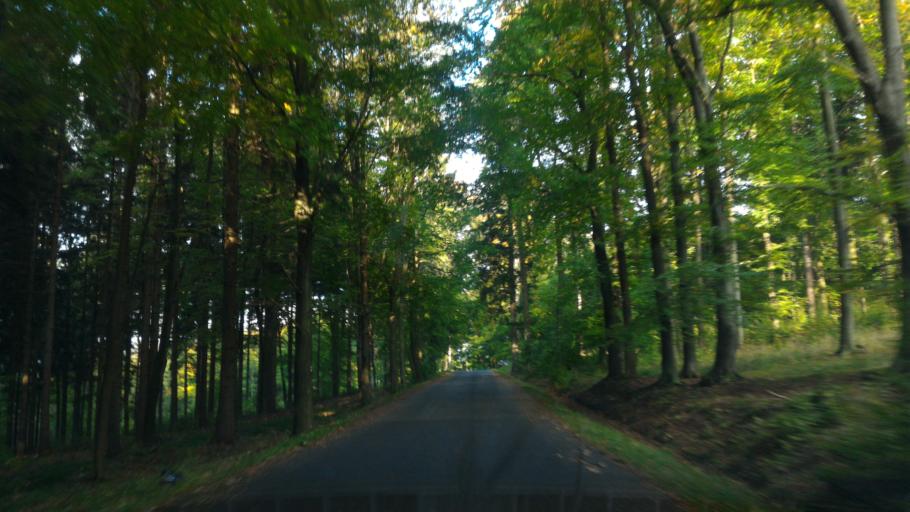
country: CZ
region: Ustecky
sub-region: Okres Decin
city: Chribska
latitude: 50.8398
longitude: 14.5006
